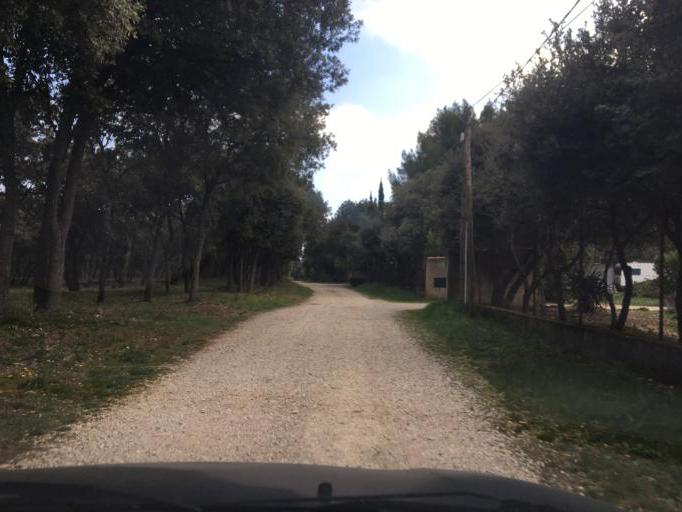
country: FR
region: Provence-Alpes-Cote d'Azur
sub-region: Departement du Vaucluse
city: Serignan-du-Comtat
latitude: 44.1851
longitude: 4.8587
